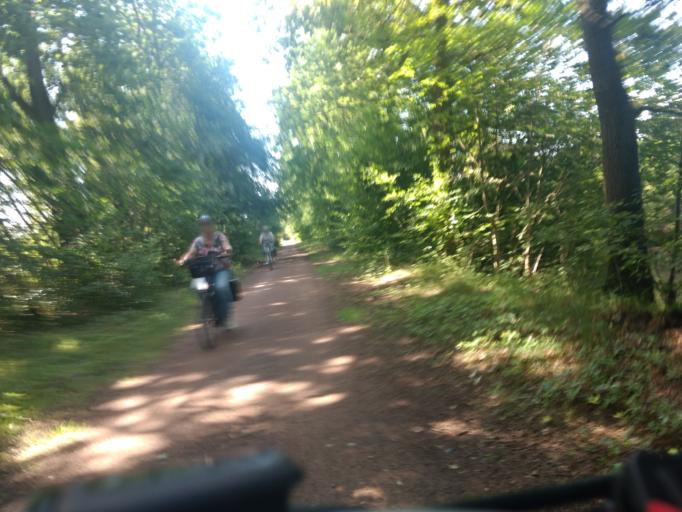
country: DE
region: North Rhine-Westphalia
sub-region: Regierungsbezirk Detmold
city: Hovelhof
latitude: 51.7667
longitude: 8.6574
